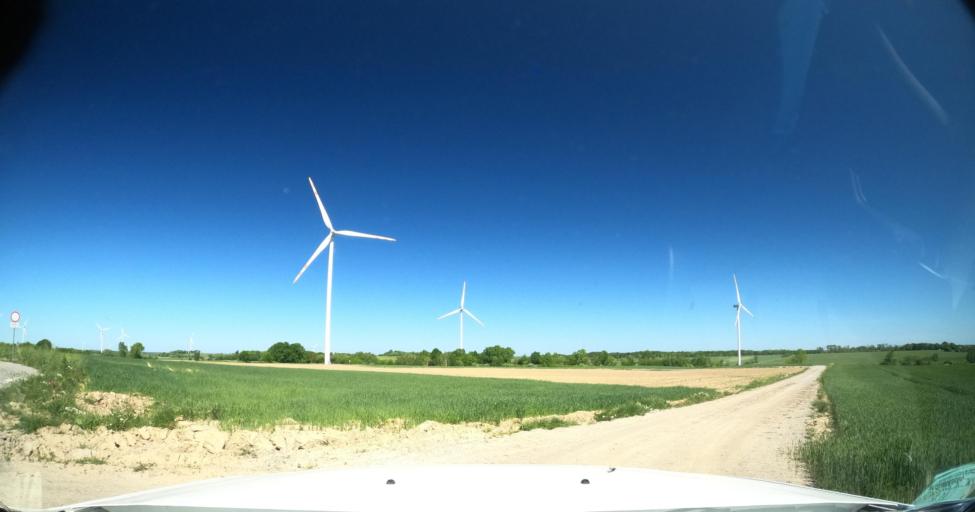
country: PL
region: Pomeranian Voivodeship
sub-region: Powiat slupski
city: Ustka
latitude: 54.5107
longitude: 16.7465
